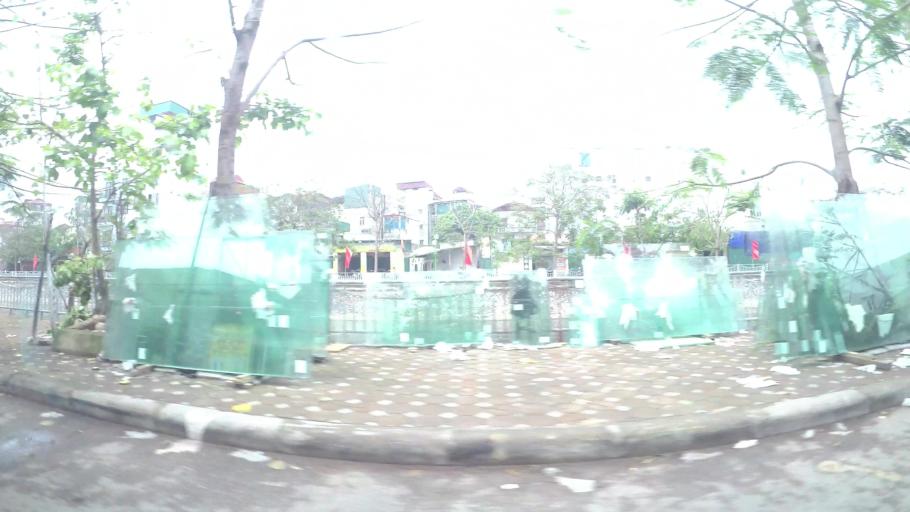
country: VN
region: Ha Noi
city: Van Dien
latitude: 20.9787
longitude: 105.8459
